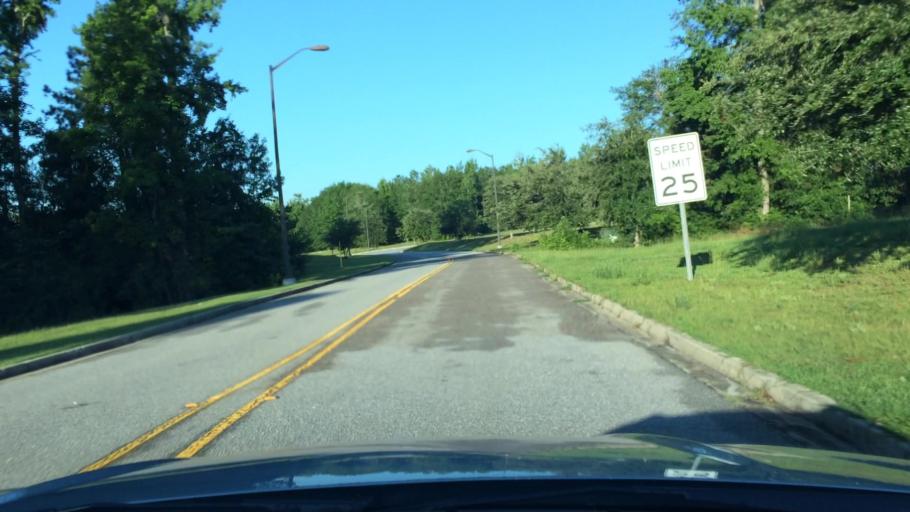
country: US
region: South Carolina
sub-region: Calhoun County
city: Oak Grove
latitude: 33.8038
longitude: -81.0036
